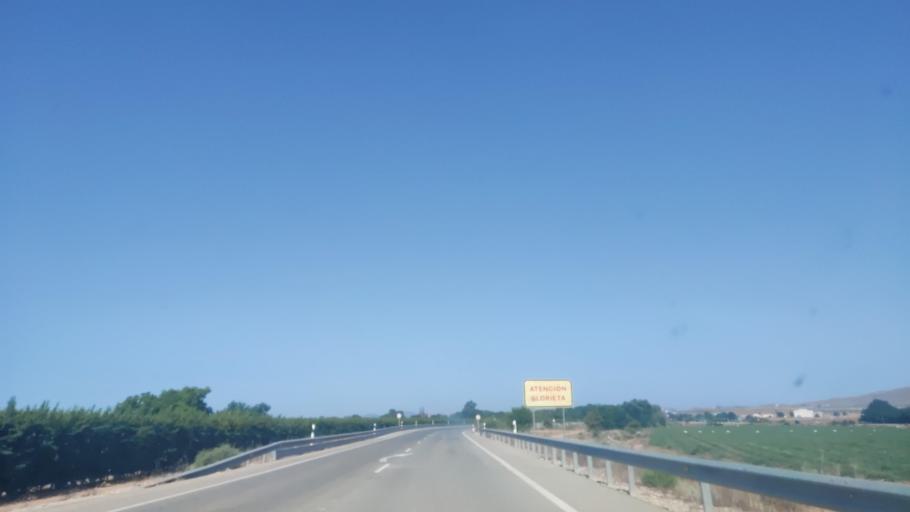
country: ES
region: Castille-La Mancha
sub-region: Provincia de Albacete
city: Hellin
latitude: 38.4926
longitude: -1.6365
